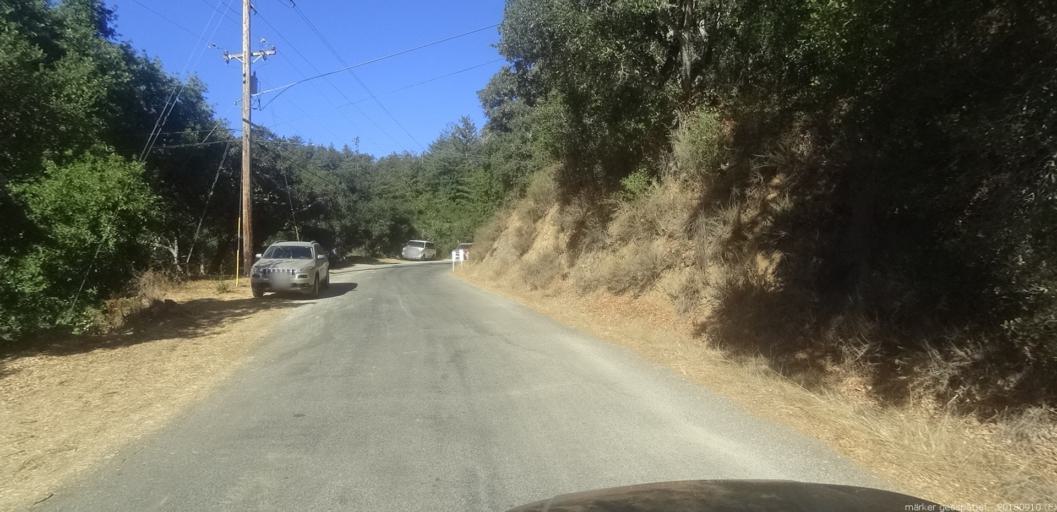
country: US
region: California
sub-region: Monterey County
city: Carmel Valley Village
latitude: 36.3864
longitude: -121.8695
